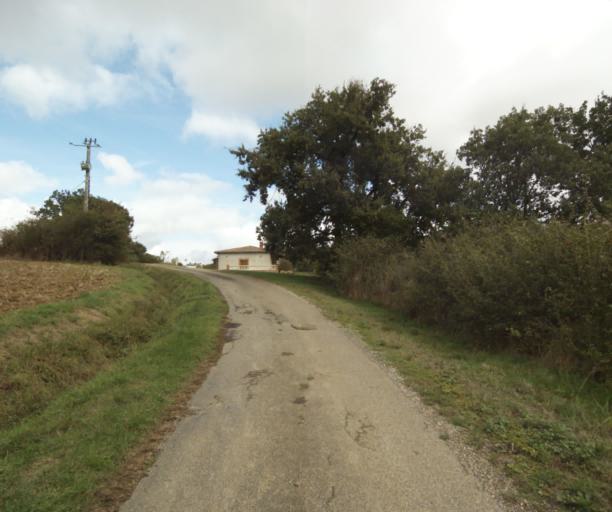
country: FR
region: Midi-Pyrenees
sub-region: Departement du Tarn-et-Garonne
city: Beaumont-de-Lomagne
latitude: 43.8699
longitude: 1.1041
